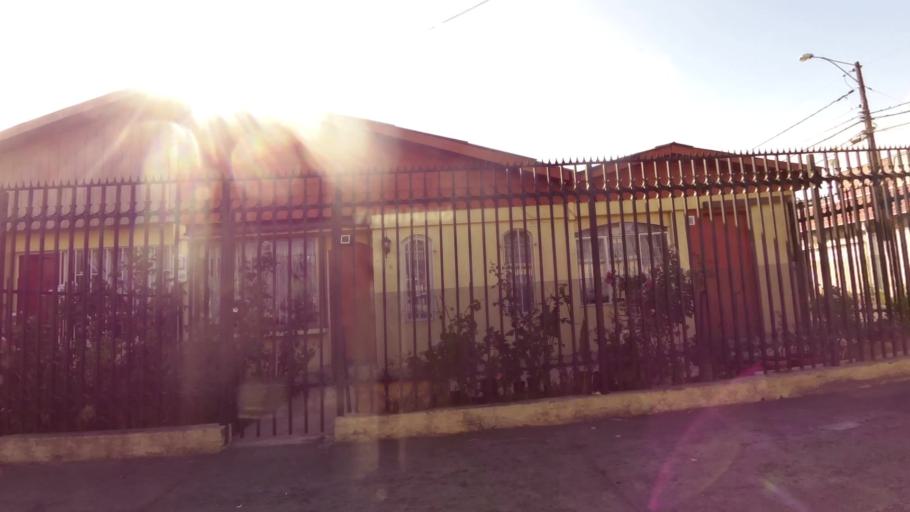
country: CL
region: Biobio
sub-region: Provincia de Concepcion
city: Concepcion
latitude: -36.7951
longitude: -73.0995
